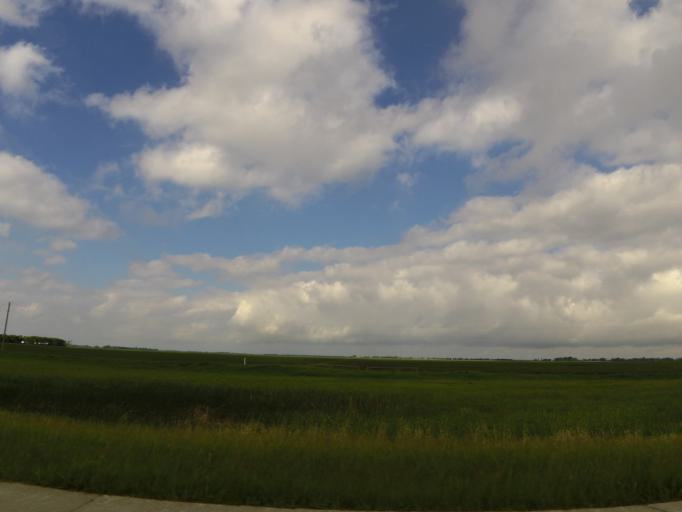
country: US
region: North Dakota
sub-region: Walsh County
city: Grafton
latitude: 48.3317
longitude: -97.1899
